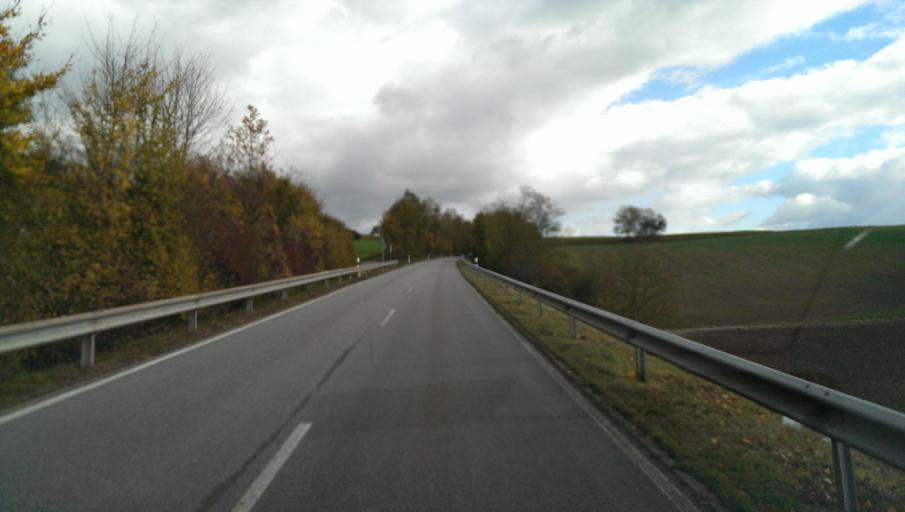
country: DE
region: Baden-Wuerttemberg
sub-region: Karlsruhe Region
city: Balzfeld
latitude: 49.2382
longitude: 8.8026
